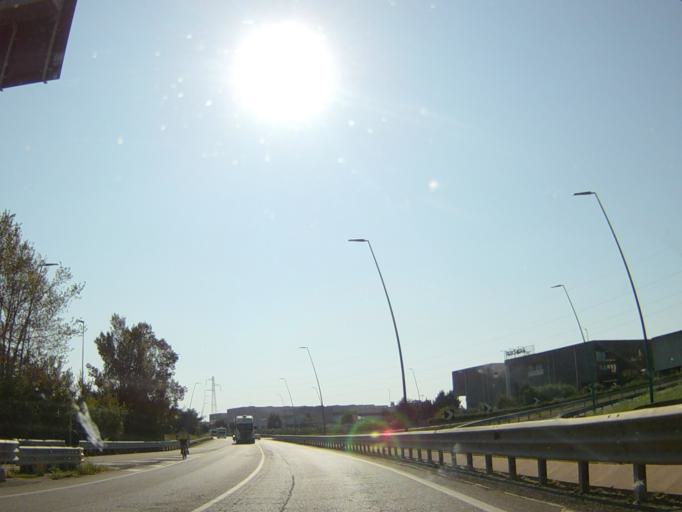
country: IT
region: Veneto
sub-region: Provincia di Verona
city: Peschiera del Garda
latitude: 45.4313
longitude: 10.6857
